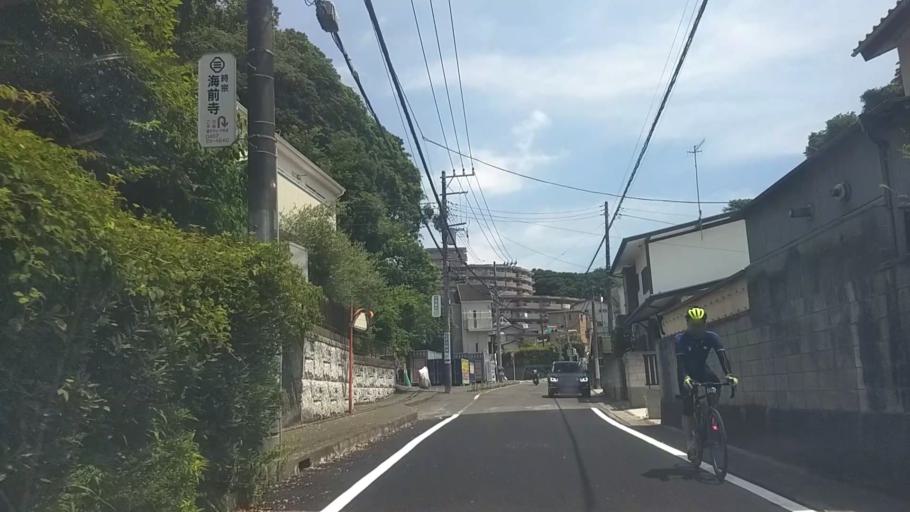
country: JP
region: Kanagawa
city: Zushi
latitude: 35.3000
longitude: 139.5642
